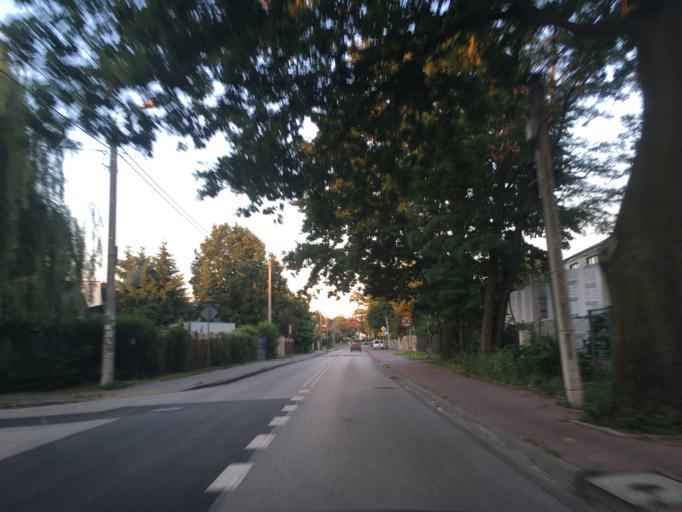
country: PL
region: Masovian Voivodeship
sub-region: Powiat piaseczynski
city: Piaseczno
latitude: 52.0639
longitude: 21.0133
